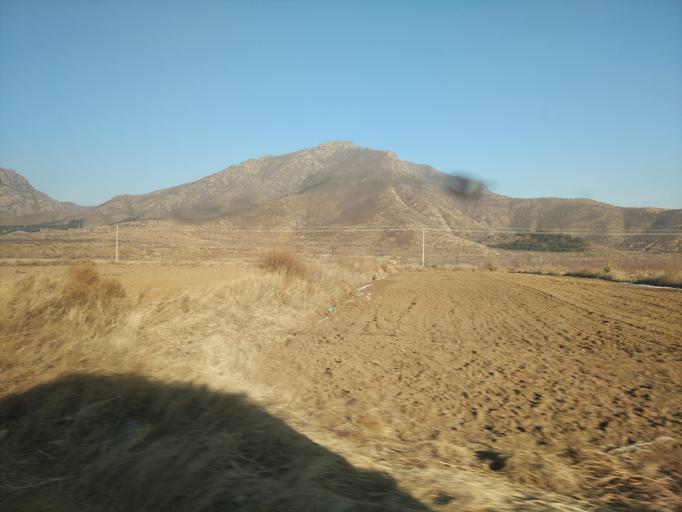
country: CN
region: Hebei
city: Xiwanzi
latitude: 40.8345
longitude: 115.5267
